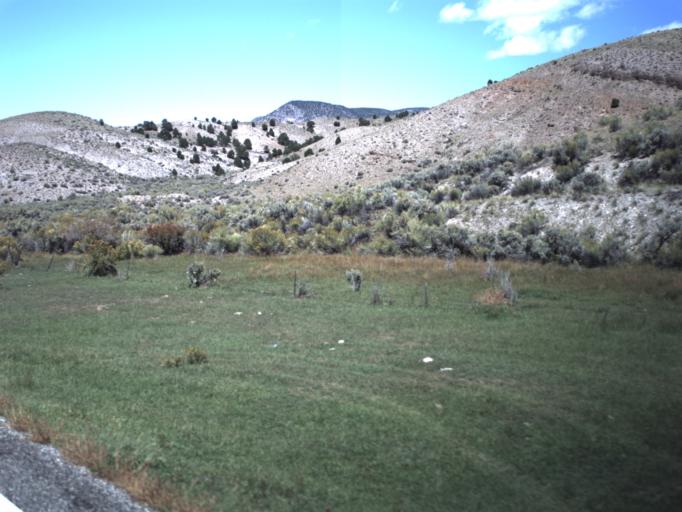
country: US
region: Utah
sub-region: Piute County
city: Junction
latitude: 38.1702
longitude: -112.0578
